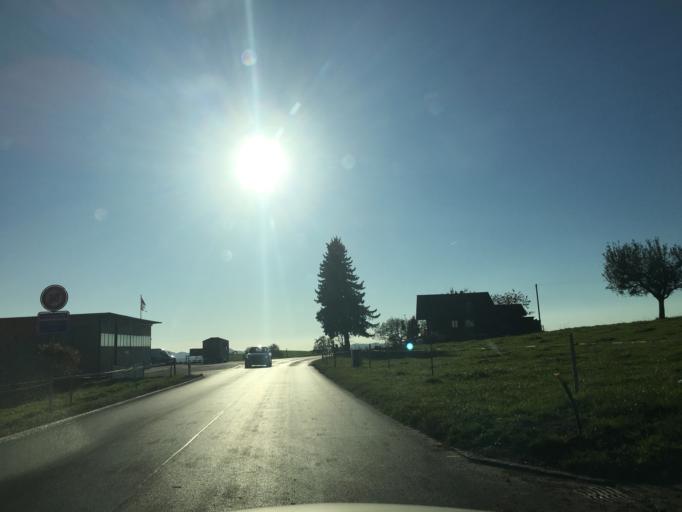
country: CH
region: Vaud
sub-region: Lavaux-Oron District
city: Oron-la-ville
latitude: 46.5760
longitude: 6.8669
